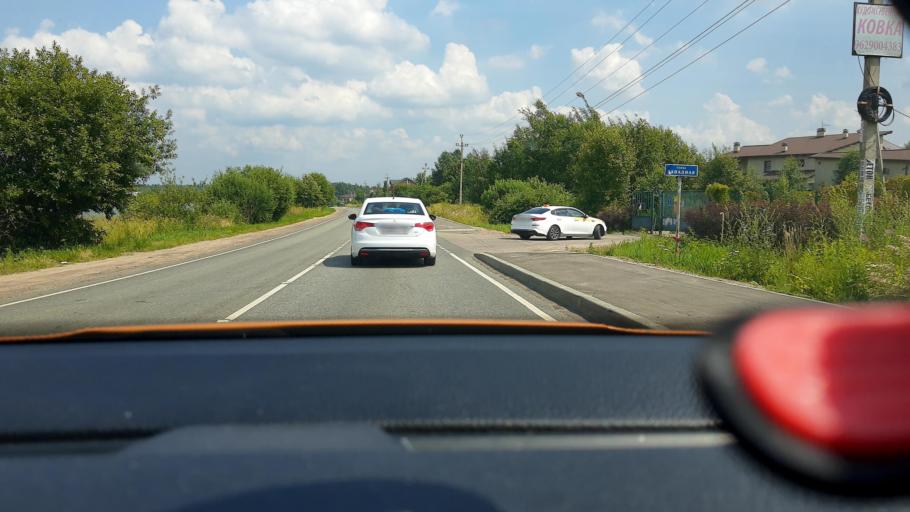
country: RU
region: Moskovskaya
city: Povedniki
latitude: 56.0081
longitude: 37.5738
